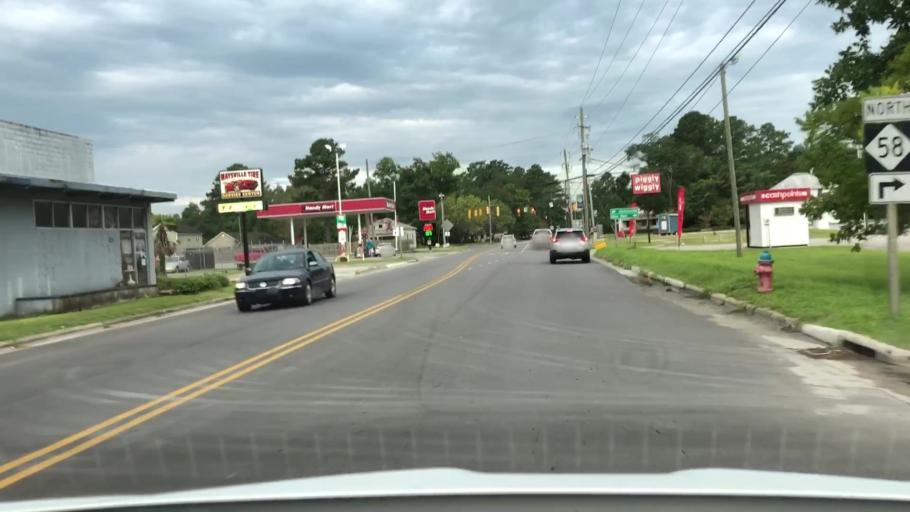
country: US
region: North Carolina
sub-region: Jones County
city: Maysville
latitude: 34.9016
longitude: -77.2300
